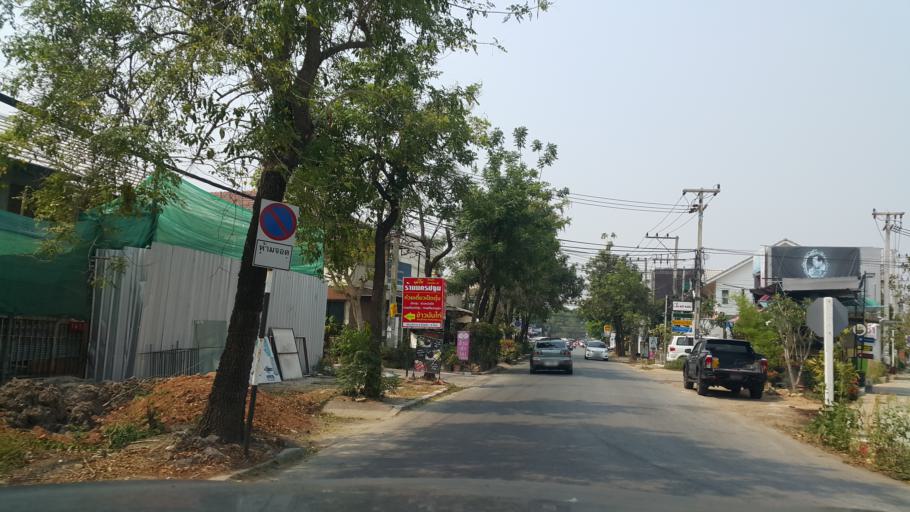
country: TH
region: Chiang Mai
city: Chiang Mai
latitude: 18.7876
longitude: 98.9625
